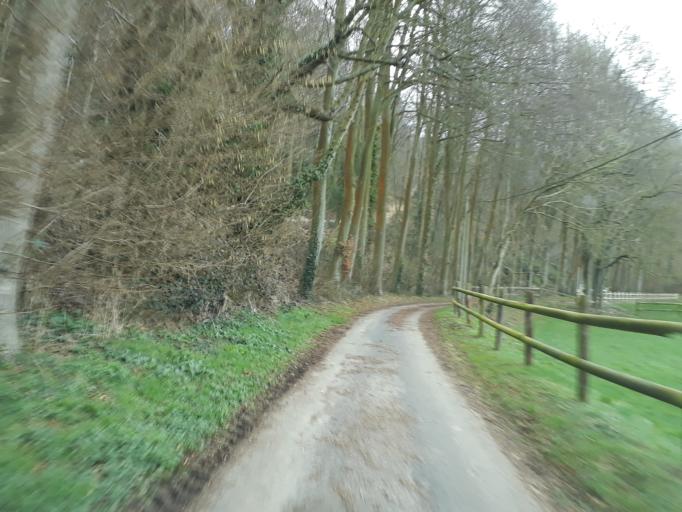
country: FR
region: Haute-Normandie
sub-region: Departement de la Seine-Maritime
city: Yport
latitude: 49.7312
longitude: 0.2940
